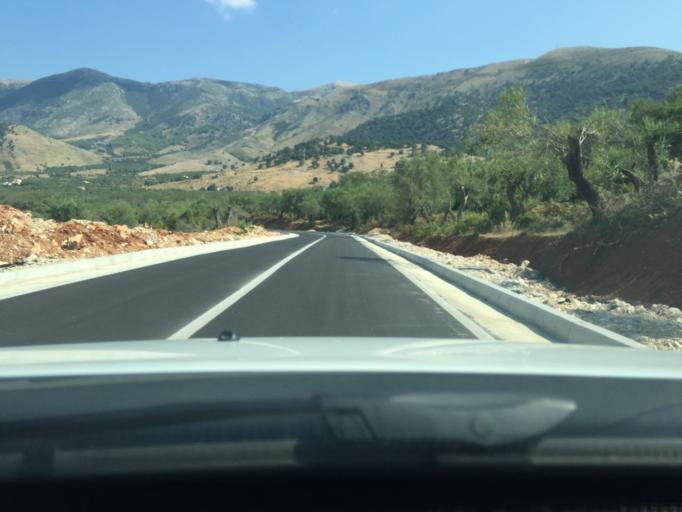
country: AL
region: Vlore
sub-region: Rrethi i Vlores
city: Himare
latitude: 40.1018
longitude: 19.7608
